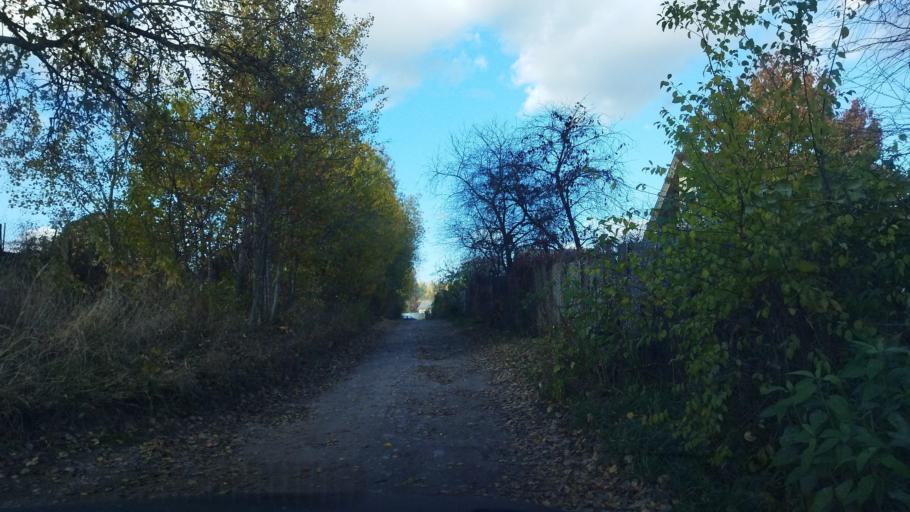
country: BY
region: Minsk
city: Slabada
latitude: 53.9871
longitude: 27.8996
